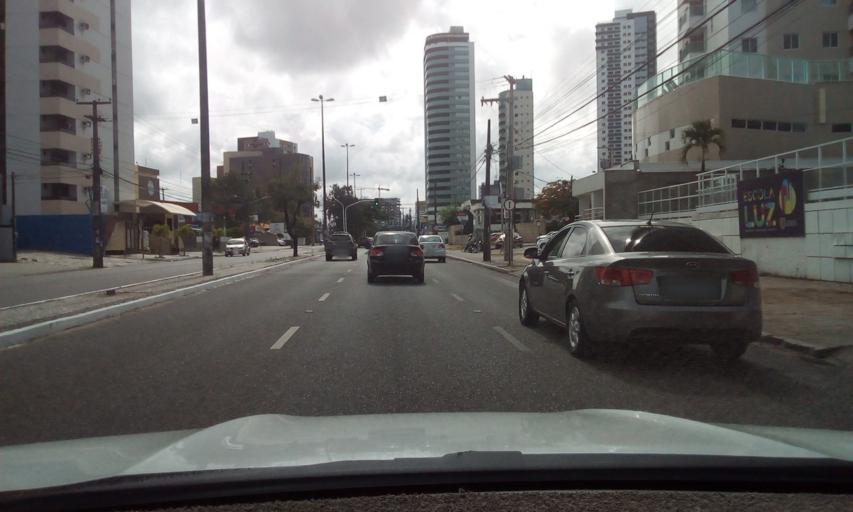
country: BR
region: Paraiba
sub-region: Joao Pessoa
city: Joao Pessoa
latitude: -7.1172
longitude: -34.8385
